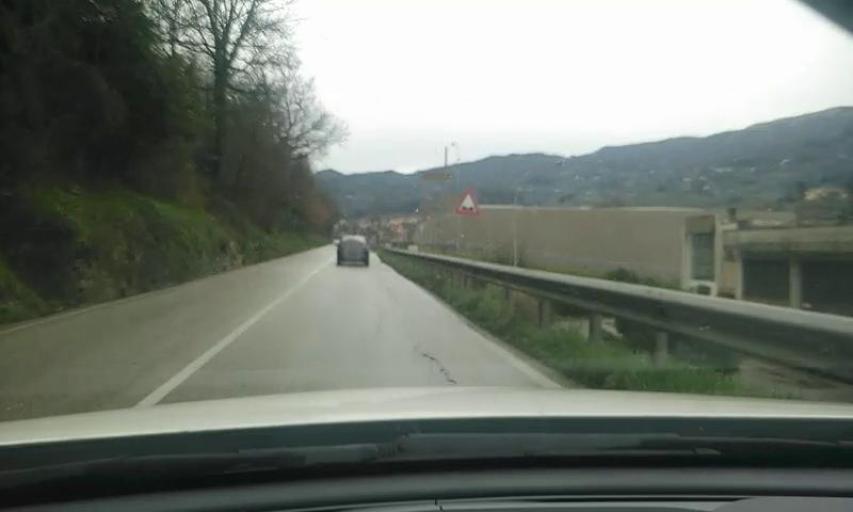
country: IT
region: Tuscany
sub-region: Provincia di Prato
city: Vaiano
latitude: 43.9505
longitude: 11.1268
